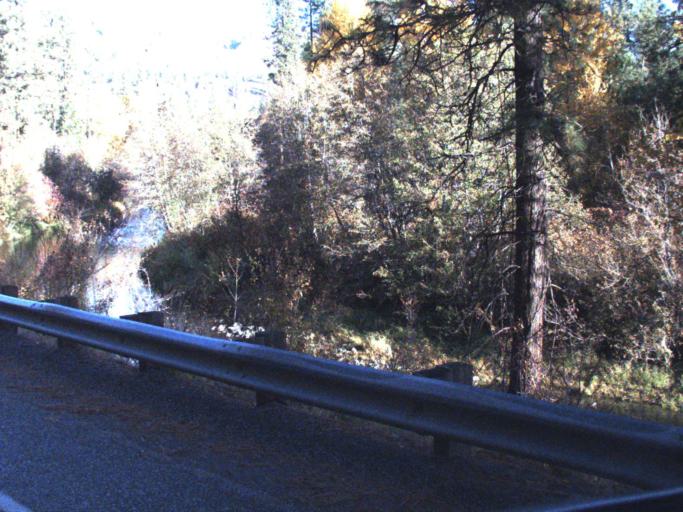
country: US
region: Washington
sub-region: Okanogan County
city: Coulee Dam
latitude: 48.1024
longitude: -118.6992
